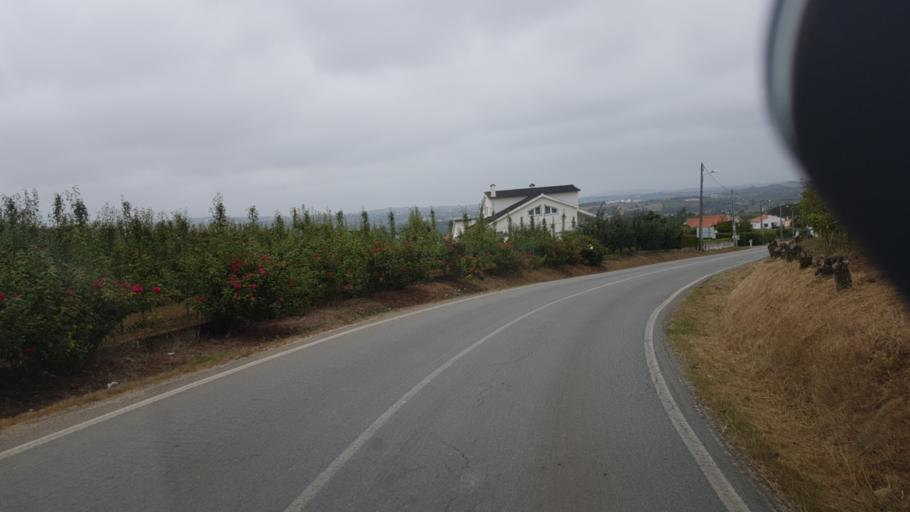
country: PT
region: Leiria
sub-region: Bombarral
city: Bombarral
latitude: 39.2759
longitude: -9.1793
